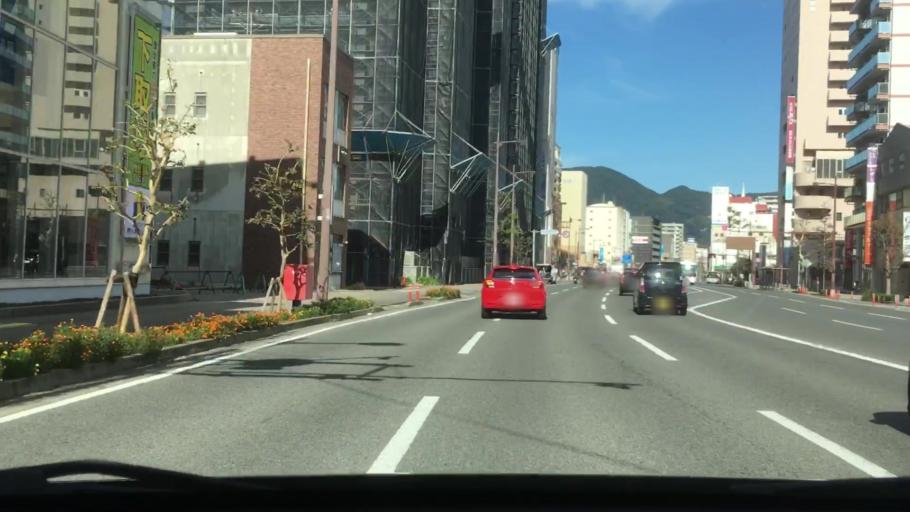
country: JP
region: Nagasaki
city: Sasebo
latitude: 33.1628
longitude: 129.7285
